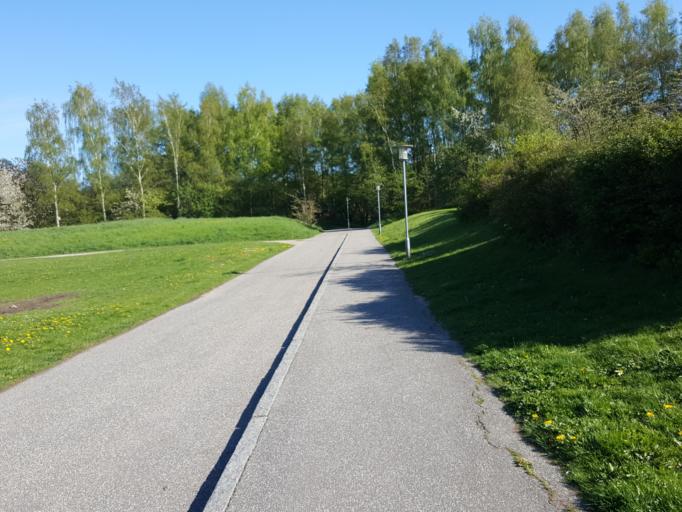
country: DK
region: Capital Region
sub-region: Rudersdal Kommune
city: Birkerod
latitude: 55.8512
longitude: 12.4503
